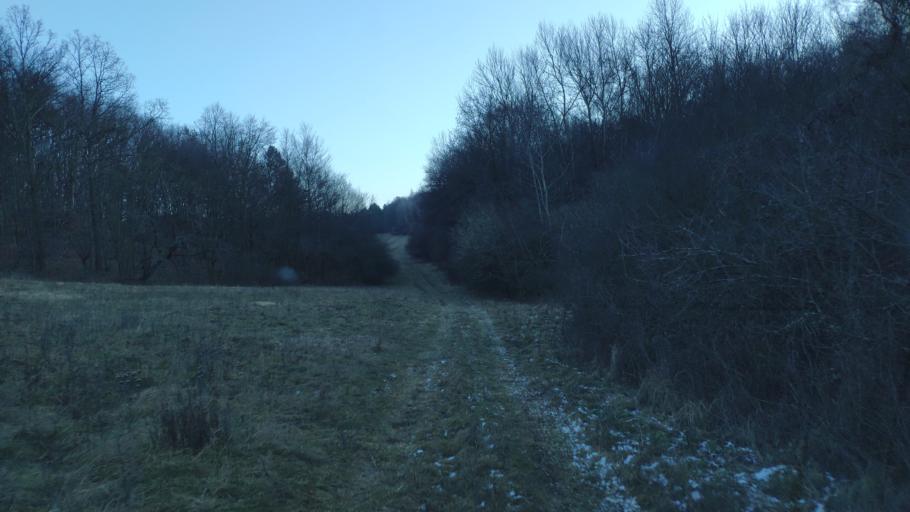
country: SK
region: Kosicky
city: Kosice
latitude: 48.8488
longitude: 21.2413
